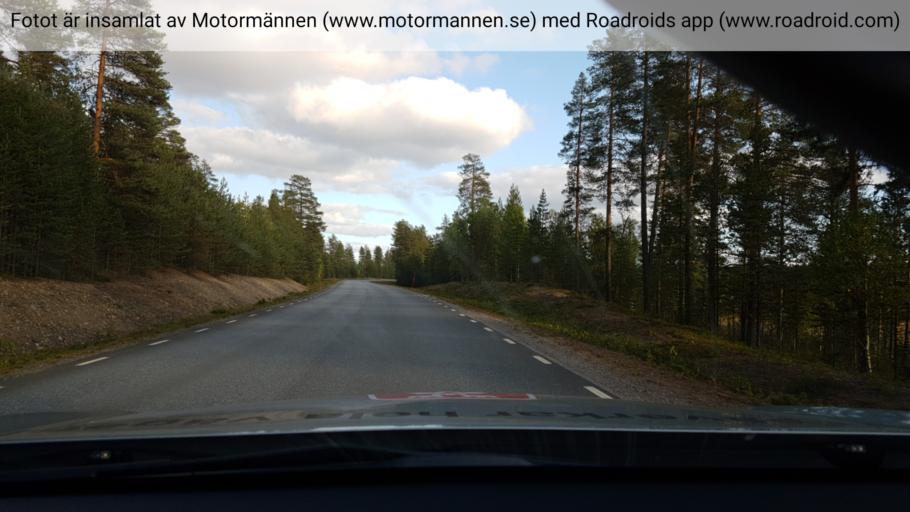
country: SE
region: Vaesterbotten
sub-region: Mala Kommun
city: Mala
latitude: 65.1456
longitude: 18.8240
